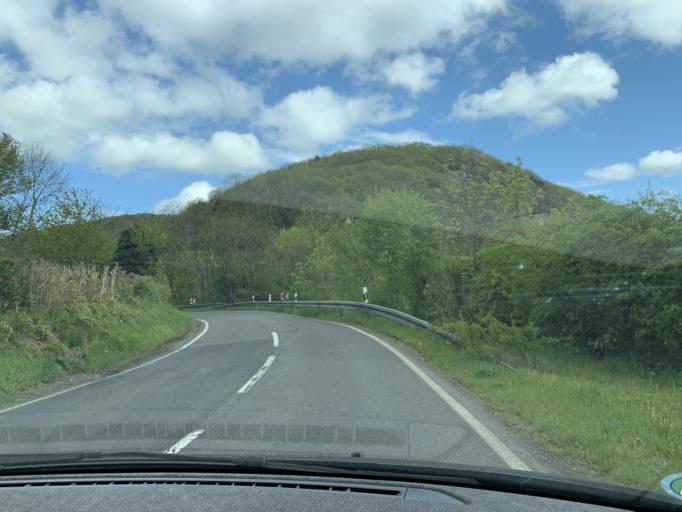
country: DE
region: North Rhine-Westphalia
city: Heimbach
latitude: 50.6395
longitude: 6.4701
